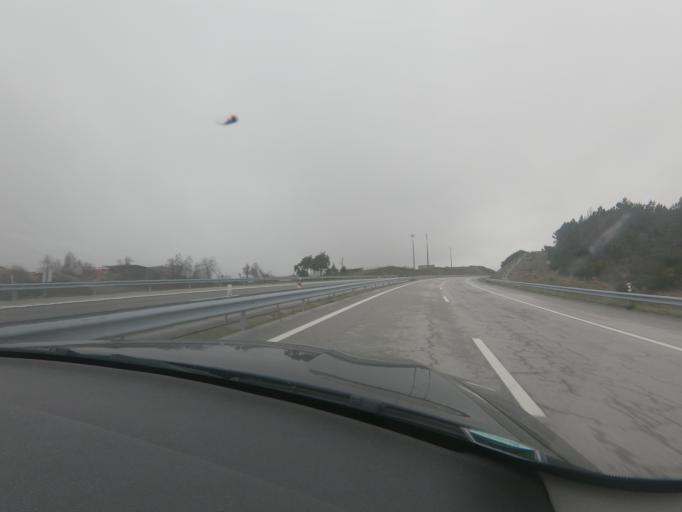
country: PT
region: Viseu
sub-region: Castro Daire
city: Castro Daire
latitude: 40.9503
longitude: -7.8944
